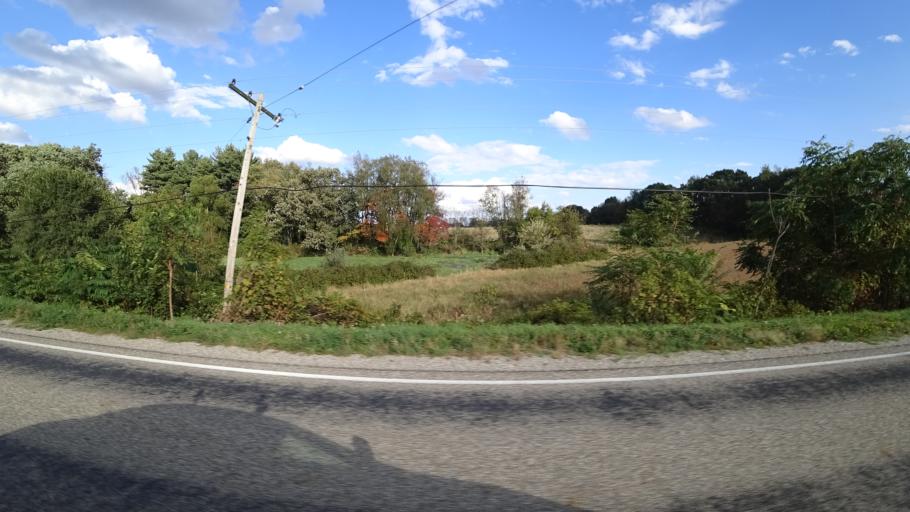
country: US
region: Michigan
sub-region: Saint Joseph County
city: Sturgis
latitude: 41.8448
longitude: -85.4287
